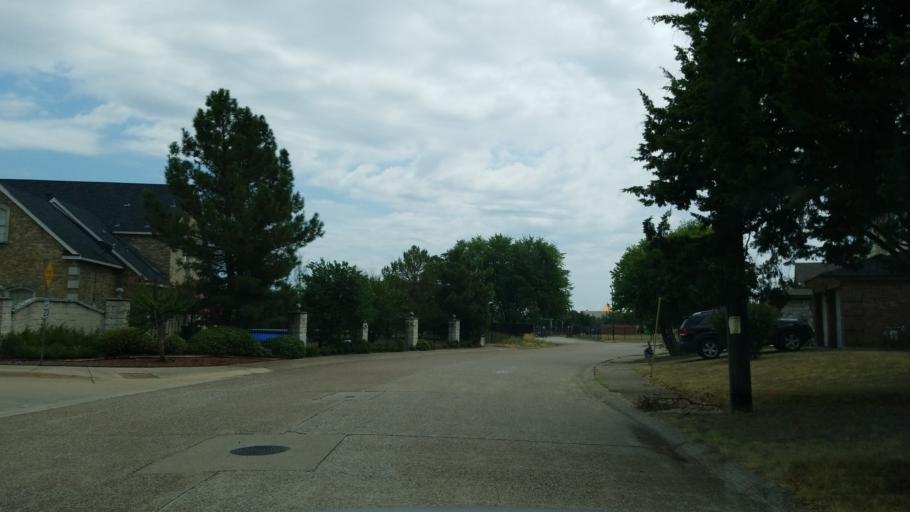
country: US
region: Texas
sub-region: Dallas County
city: Duncanville
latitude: 32.6578
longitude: -96.8534
